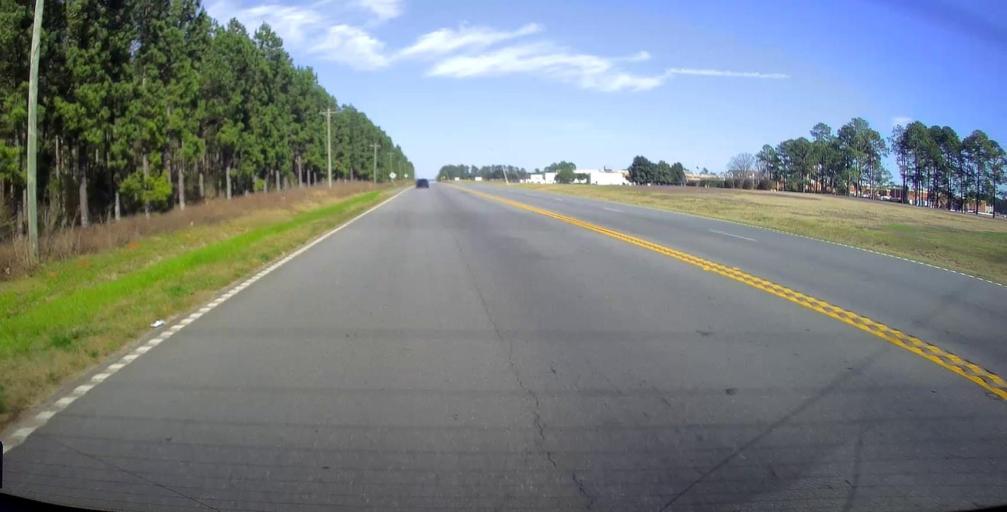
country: US
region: Georgia
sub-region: Houston County
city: Perry
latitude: 32.4410
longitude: -83.6351
